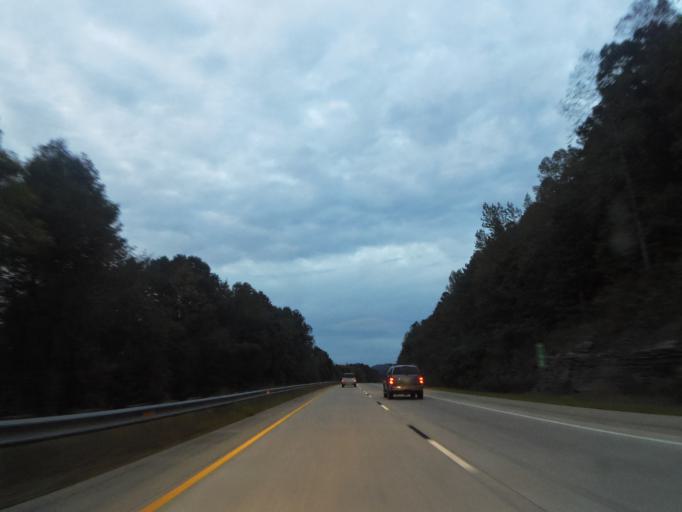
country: US
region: Alabama
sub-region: Etowah County
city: Gadsden
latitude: 34.0960
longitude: -86.0067
